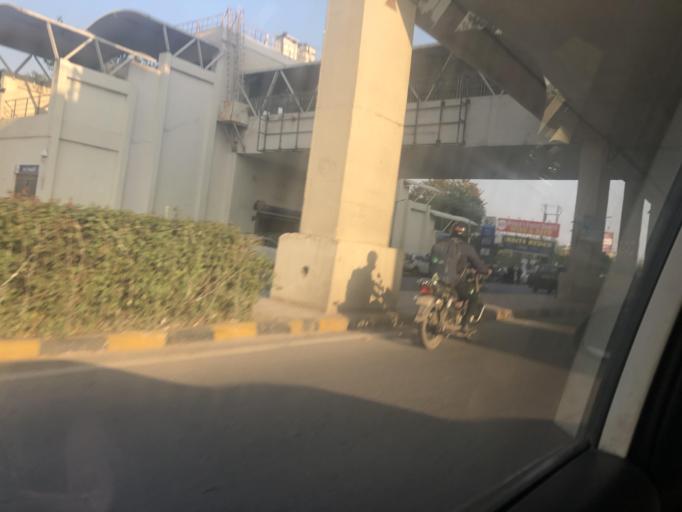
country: IN
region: Haryana
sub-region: Gurgaon
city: Gurgaon
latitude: 28.4880
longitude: 77.0925
